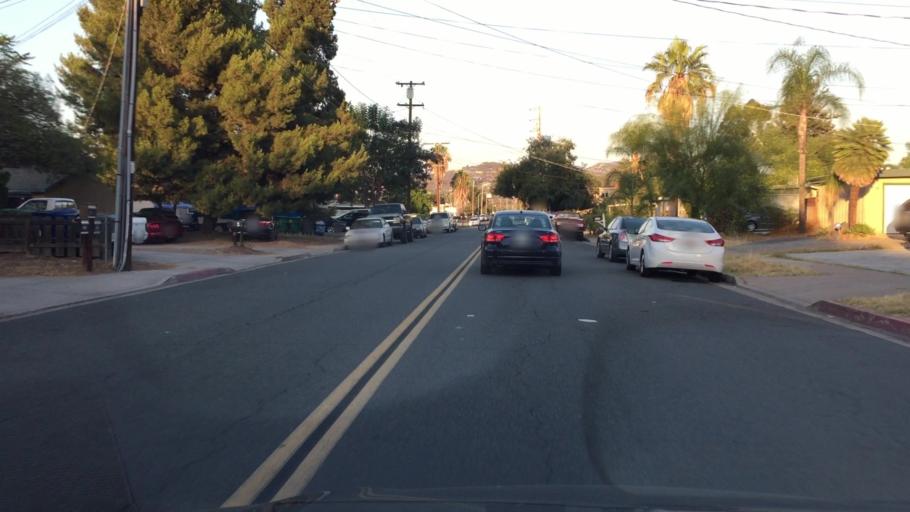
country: US
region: California
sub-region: San Diego County
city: Bostonia
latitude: 32.8040
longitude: -116.9417
